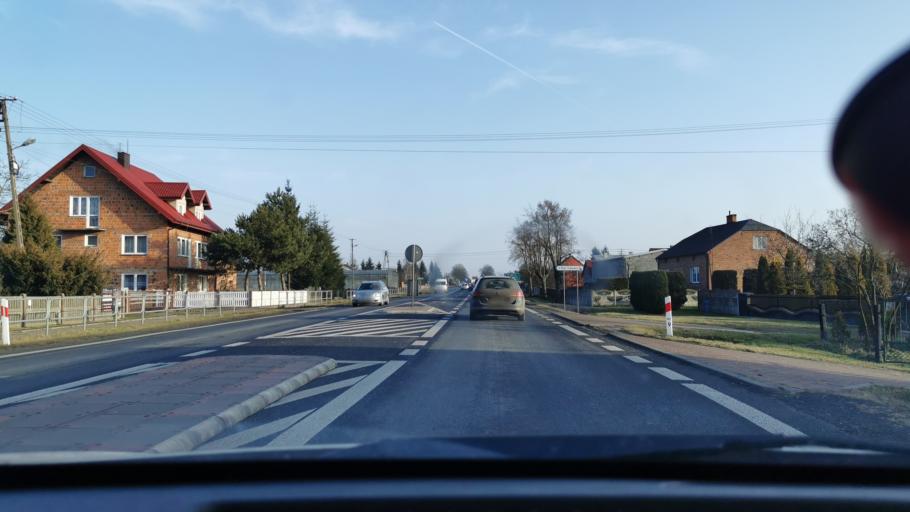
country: PL
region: Lodz Voivodeship
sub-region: Powiat sieradzki
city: Wroblew
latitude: 51.6308
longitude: 18.5492
